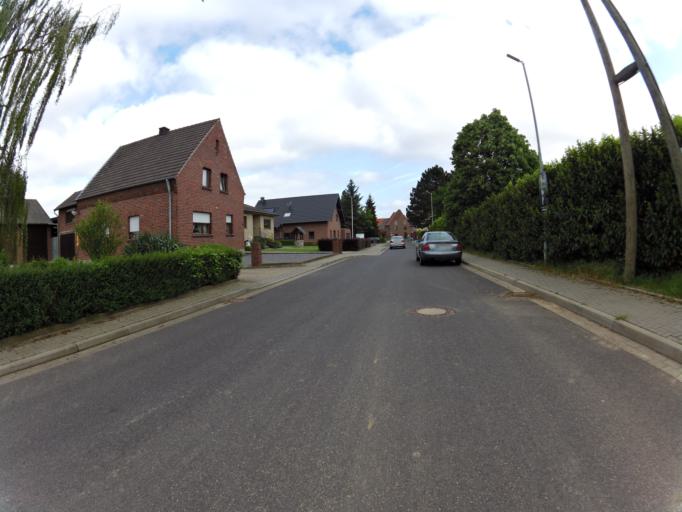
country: DE
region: North Rhine-Westphalia
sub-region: Regierungsbezirk Koln
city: Linnich
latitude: 50.9437
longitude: 6.2482
